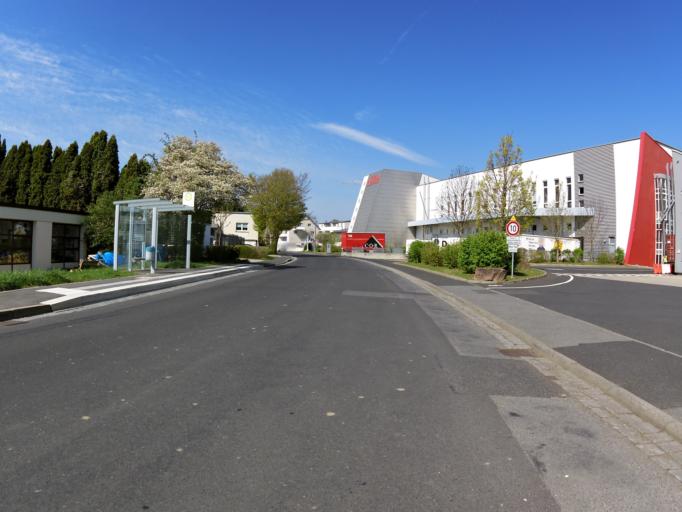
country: DE
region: Bavaria
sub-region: Regierungsbezirk Unterfranken
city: Rottendorf
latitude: 49.7909
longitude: 10.0335
